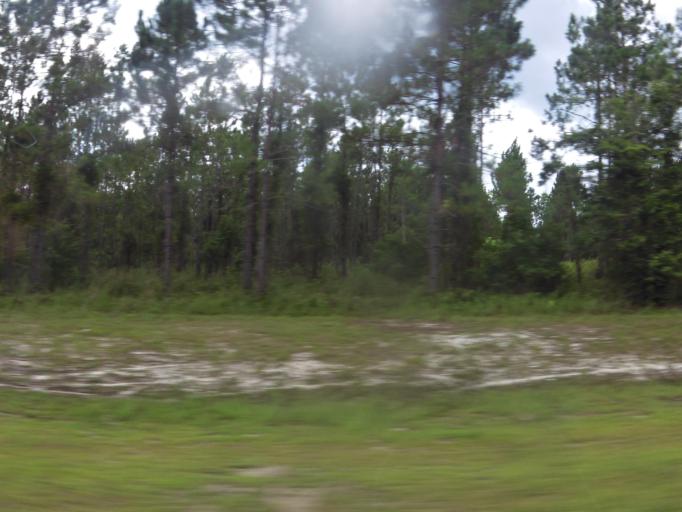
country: US
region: Georgia
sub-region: Camden County
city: Kingsland
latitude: 30.7651
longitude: -81.6495
